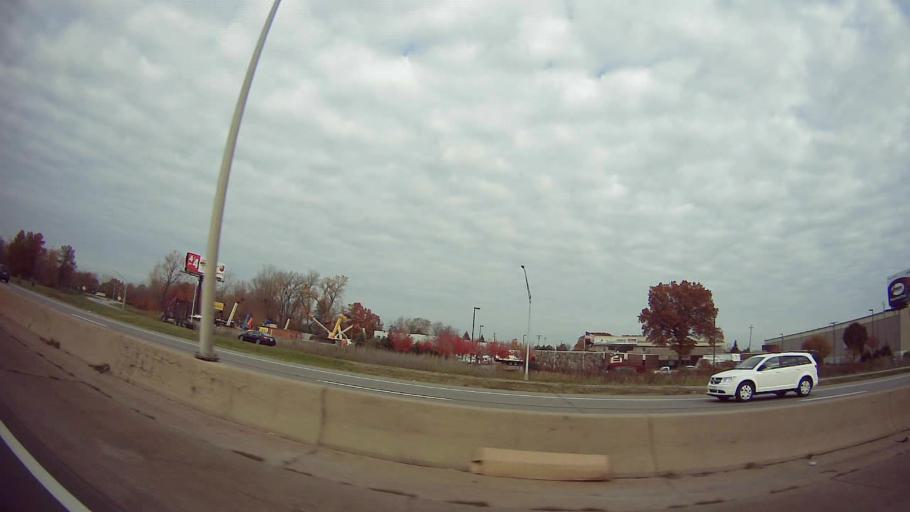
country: US
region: Michigan
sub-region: Wayne County
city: Inkster
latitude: 42.2440
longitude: -83.3226
